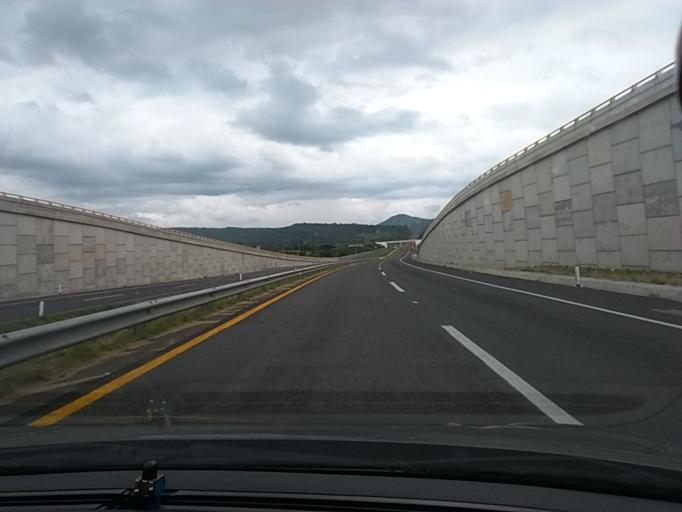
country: MX
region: Jalisco
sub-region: Zapotlanejo
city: La Mezquitera
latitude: 20.5467
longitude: -103.0321
